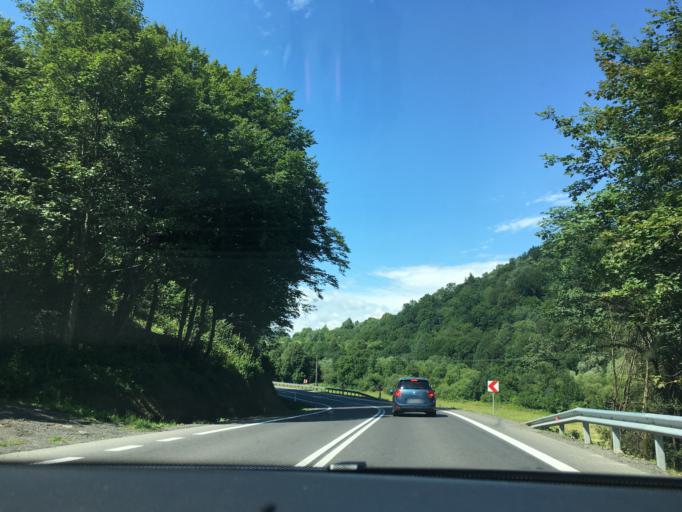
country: PL
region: Subcarpathian Voivodeship
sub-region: Powiat krosnienski
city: Dukla
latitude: 49.5176
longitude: 21.6932
